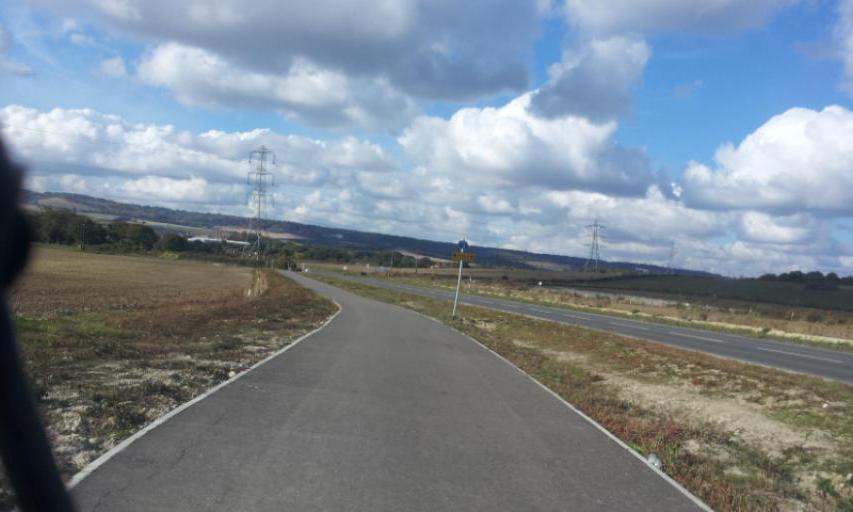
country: GB
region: England
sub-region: Kent
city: Snodland
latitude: 51.3314
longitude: 0.4693
